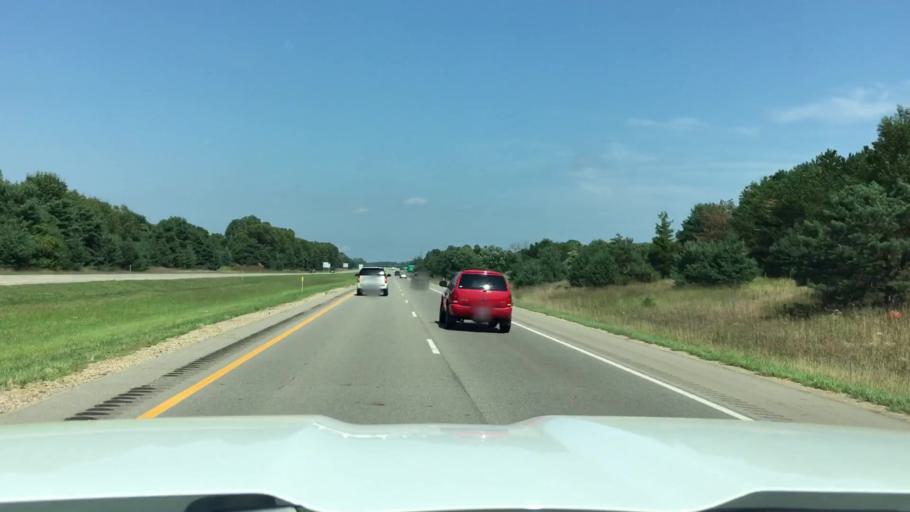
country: US
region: Michigan
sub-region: Kalamazoo County
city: Portage
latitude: 42.2122
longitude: -85.6427
